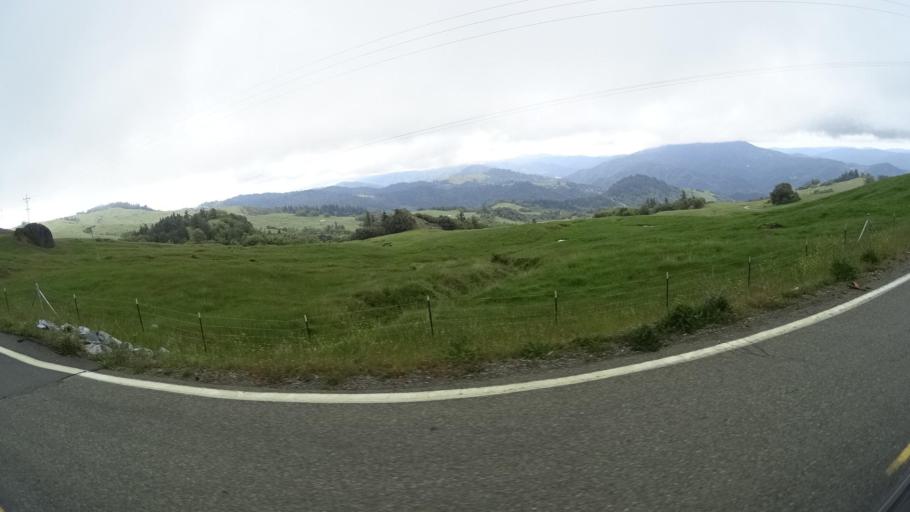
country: US
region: California
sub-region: Humboldt County
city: Redway
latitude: 40.1046
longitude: -123.7088
